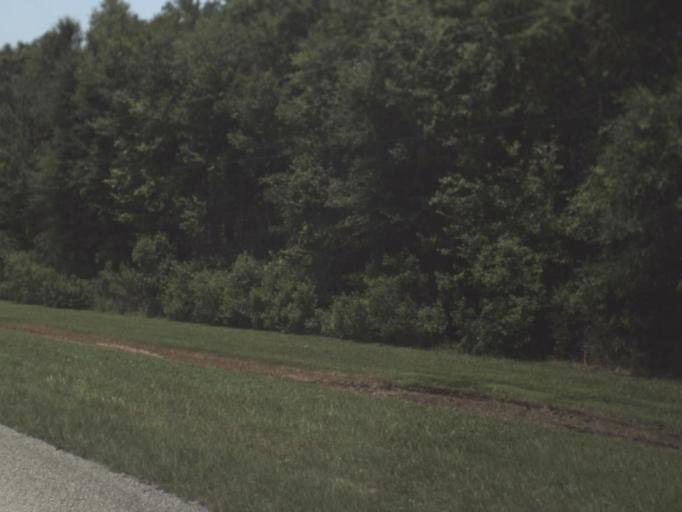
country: US
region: Florida
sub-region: Duval County
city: Baldwin
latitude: 30.1882
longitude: -82.0200
